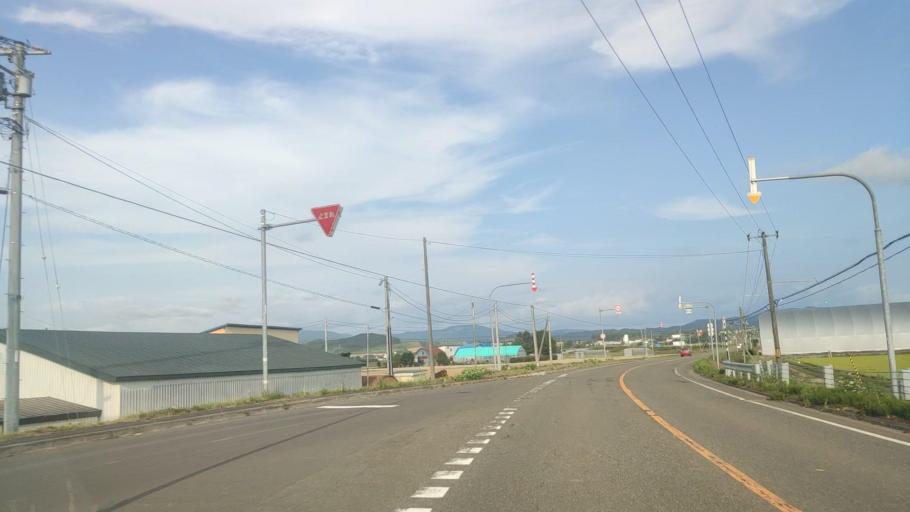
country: JP
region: Hokkaido
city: Iwamizawa
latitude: 43.0283
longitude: 141.8157
